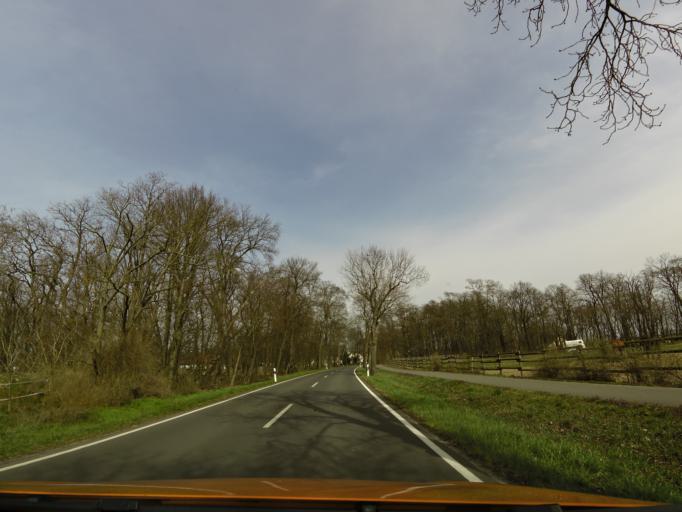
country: DE
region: Brandenburg
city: Stahnsdorf
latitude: 52.3378
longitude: 13.1881
